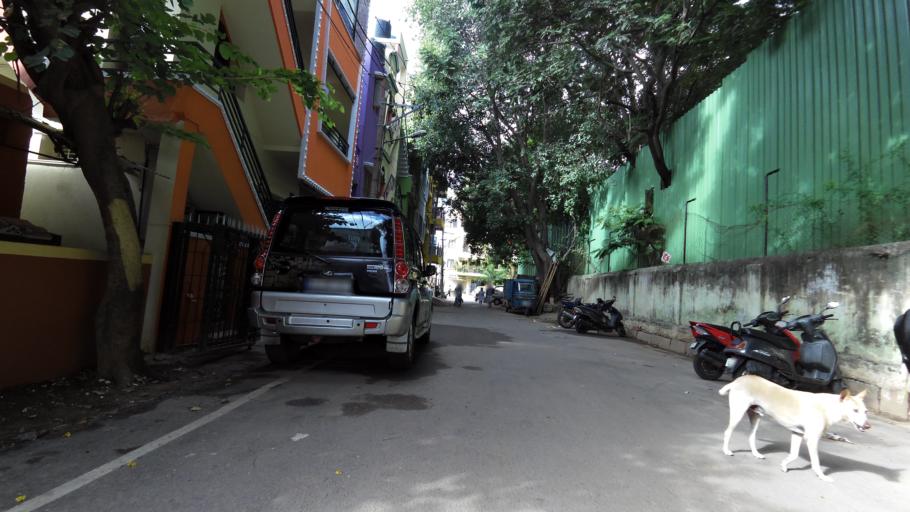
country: IN
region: Karnataka
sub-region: Bangalore Urban
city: Bangalore
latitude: 12.9984
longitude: 77.6291
